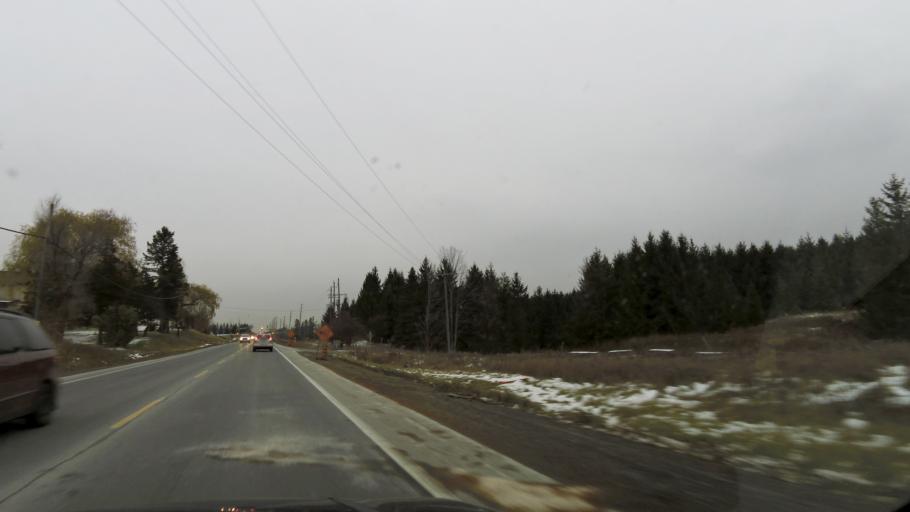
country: CA
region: Ontario
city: Vaughan
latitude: 43.8678
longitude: -79.6446
